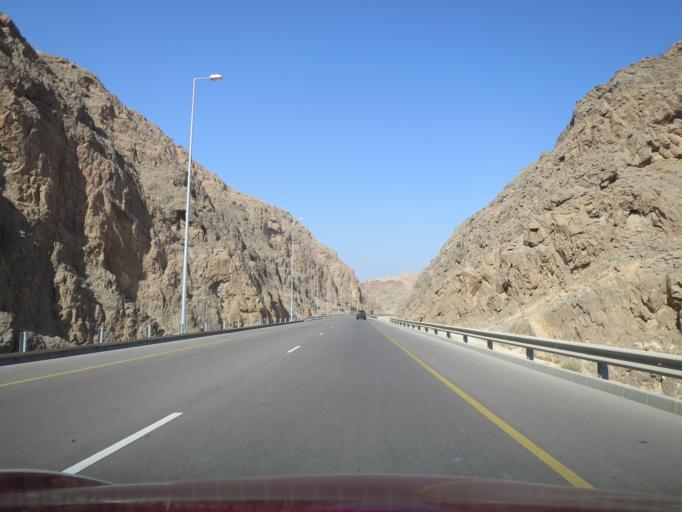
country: OM
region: Muhafazat Masqat
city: Muscat
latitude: 23.5267
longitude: 58.6431
